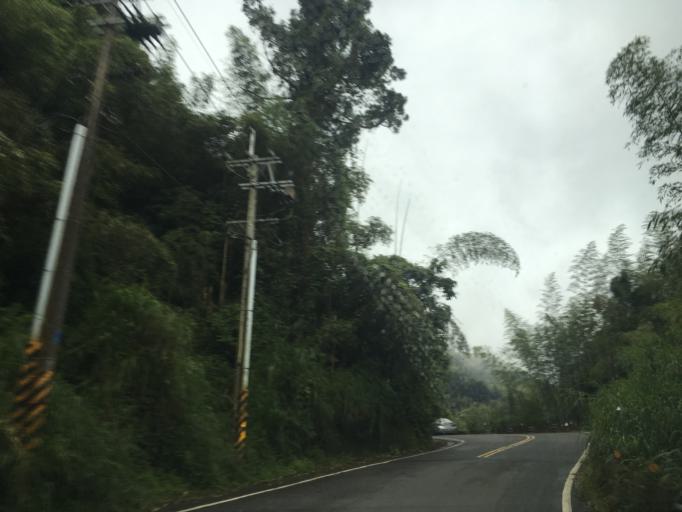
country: TW
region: Taiwan
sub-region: Chiayi
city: Jiayi Shi
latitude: 23.4888
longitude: 120.6984
